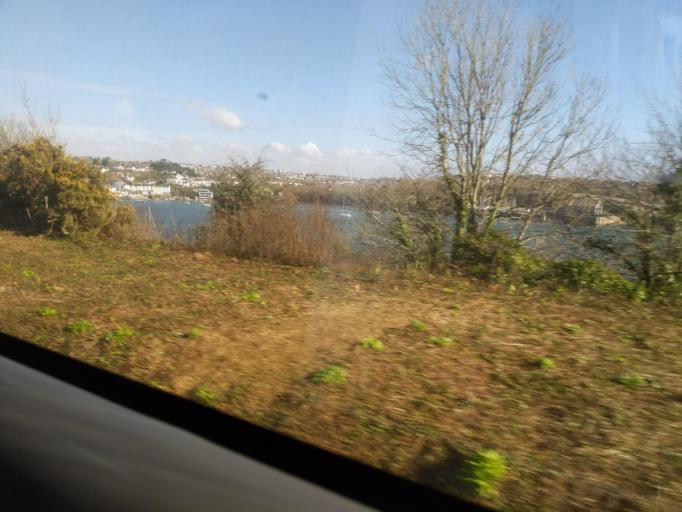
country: GB
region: England
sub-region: Cornwall
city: Saltash
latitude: 50.4009
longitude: -4.2119
